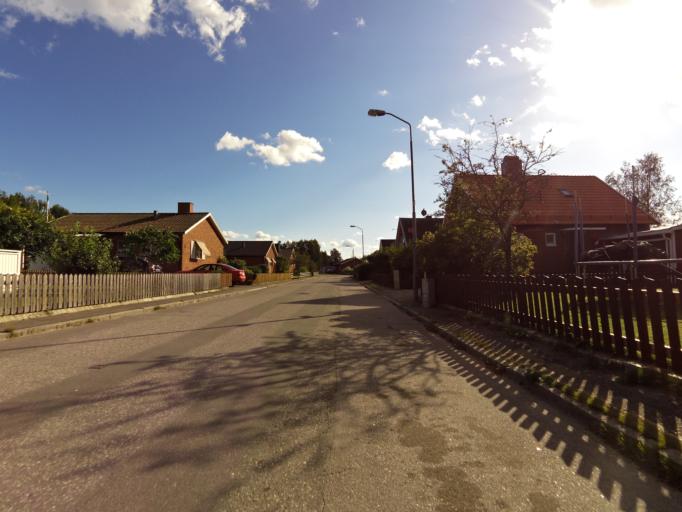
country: SE
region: Gaevleborg
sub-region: Gavle Kommun
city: Gavle
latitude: 60.7052
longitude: 17.1690
